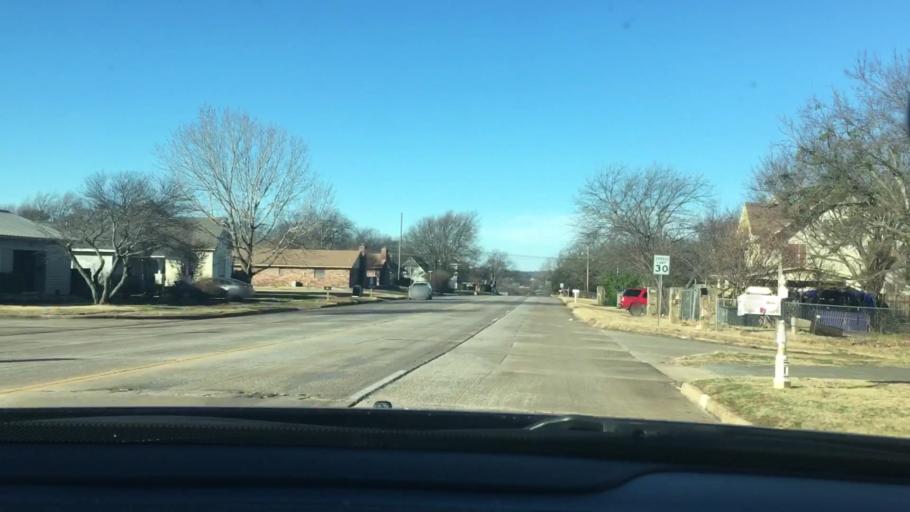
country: US
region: Oklahoma
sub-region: Murray County
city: Sulphur
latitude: 34.5110
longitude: -96.9622
